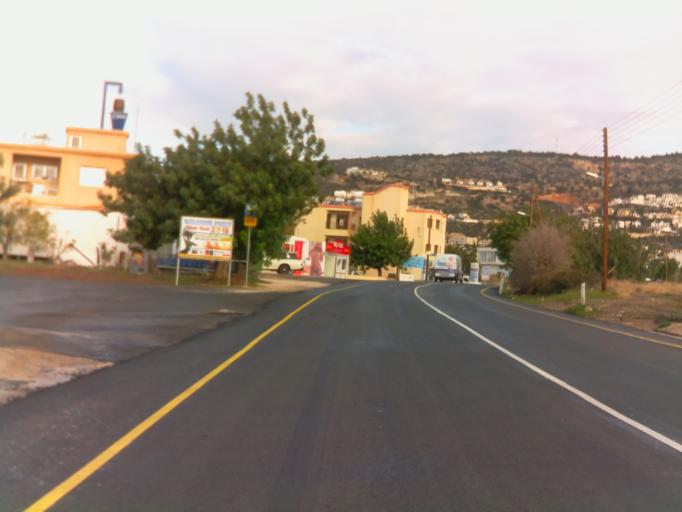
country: CY
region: Pafos
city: Pegeia
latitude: 34.8710
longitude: 32.3782
